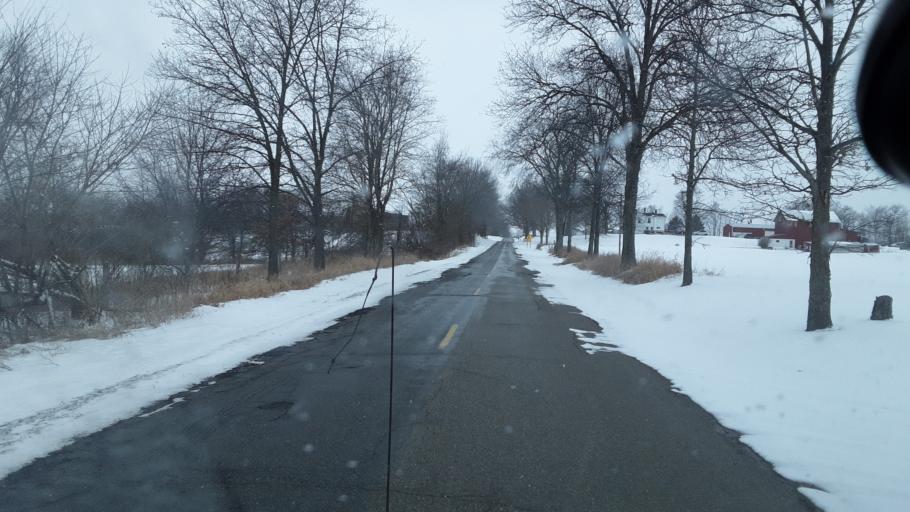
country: US
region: Michigan
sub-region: Ingham County
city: Leslie
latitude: 42.4367
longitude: -84.4587
